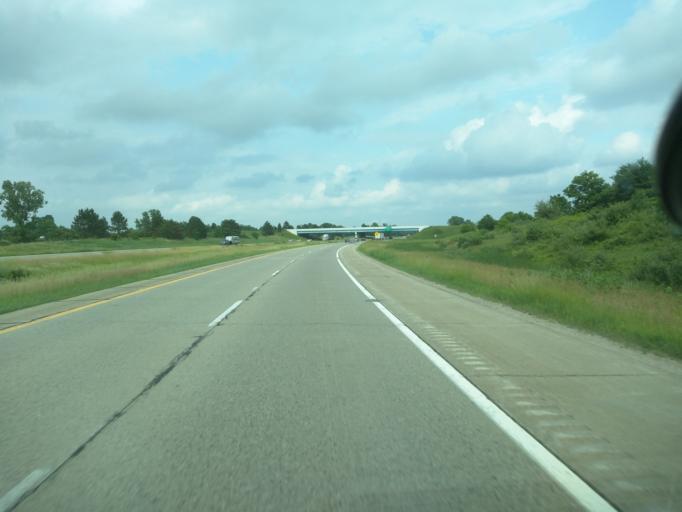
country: US
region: Michigan
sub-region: Clinton County
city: DeWitt
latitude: 42.8154
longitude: -84.5766
